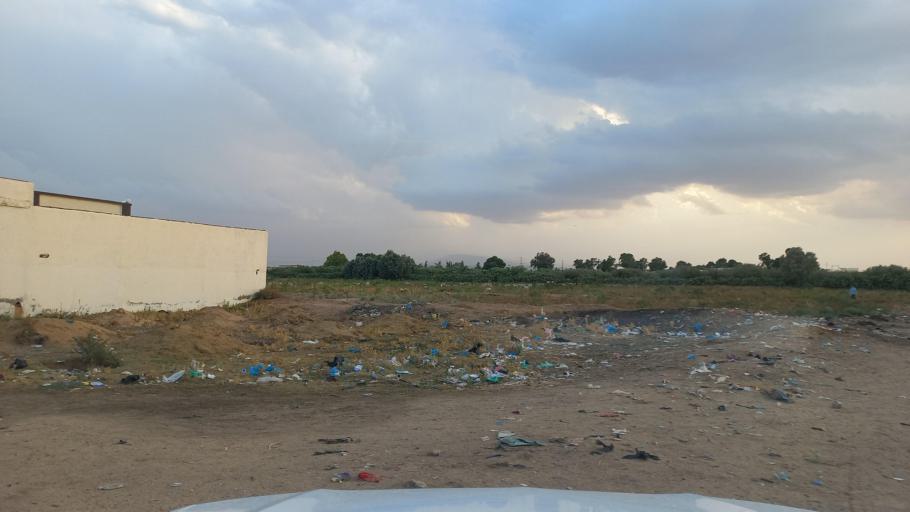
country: TN
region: Al Qasrayn
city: Kasserine
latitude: 35.2690
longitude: 9.0629
